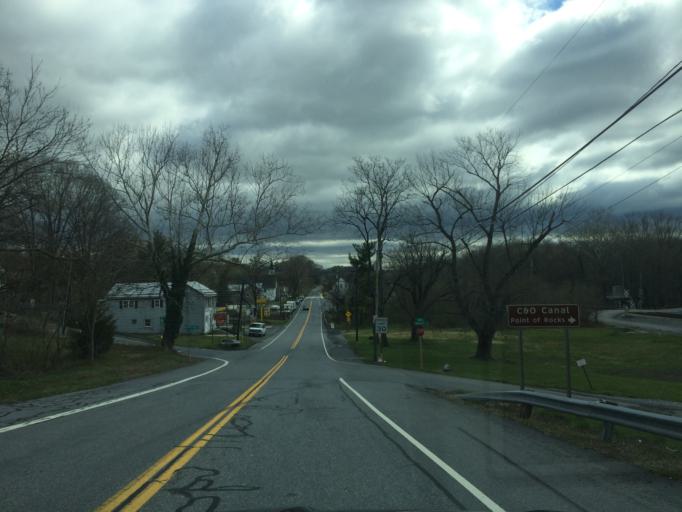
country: US
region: Maryland
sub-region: Frederick County
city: Point of Rocks
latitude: 39.2746
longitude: -77.5415
